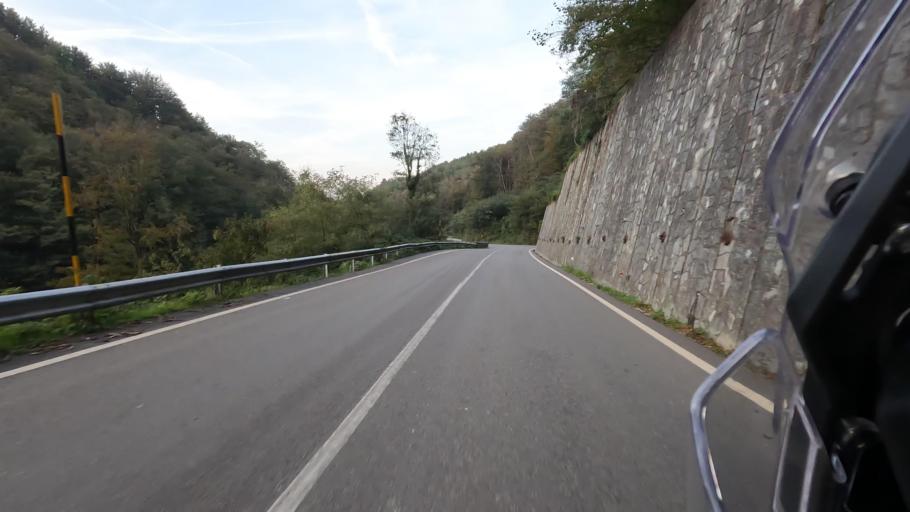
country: IT
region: Liguria
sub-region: Provincia di Savona
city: Osteria dei Cacciatori-Stella
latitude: 44.4537
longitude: 8.4793
